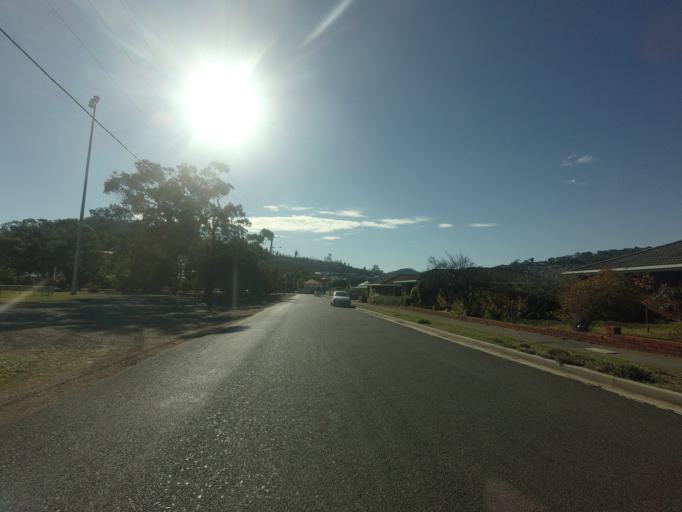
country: AU
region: Tasmania
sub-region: Clarence
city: Lindisfarne
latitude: -42.8494
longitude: 147.3516
